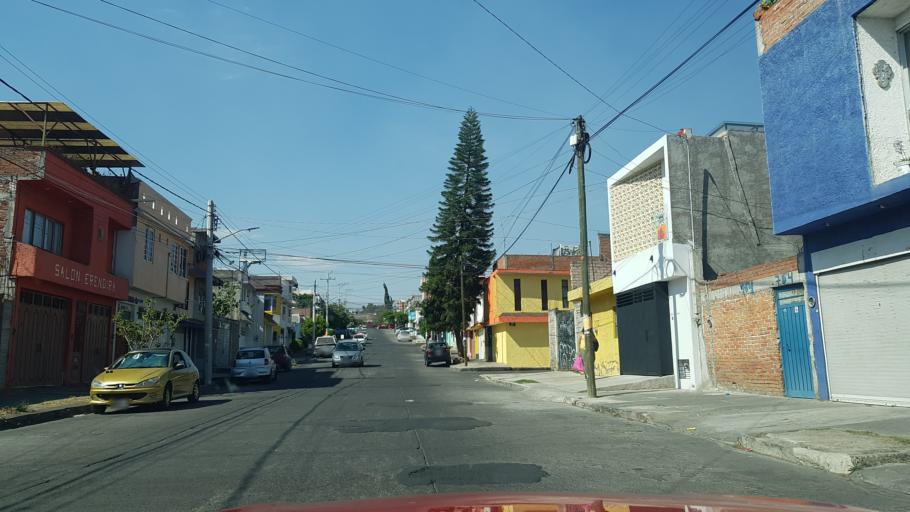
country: MX
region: Michoacan
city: Morelia
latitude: 19.7042
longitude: -101.1661
